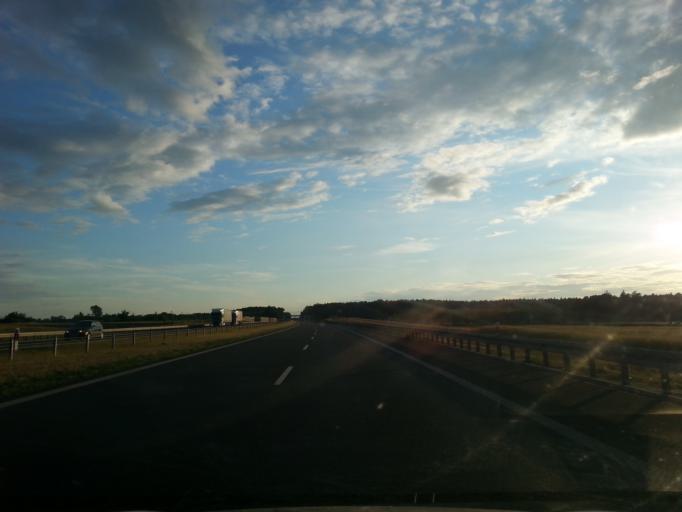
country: PL
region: Lodz Voivodeship
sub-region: Powiat wieruszowski
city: Sokolniki
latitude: 51.3235
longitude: 18.3192
